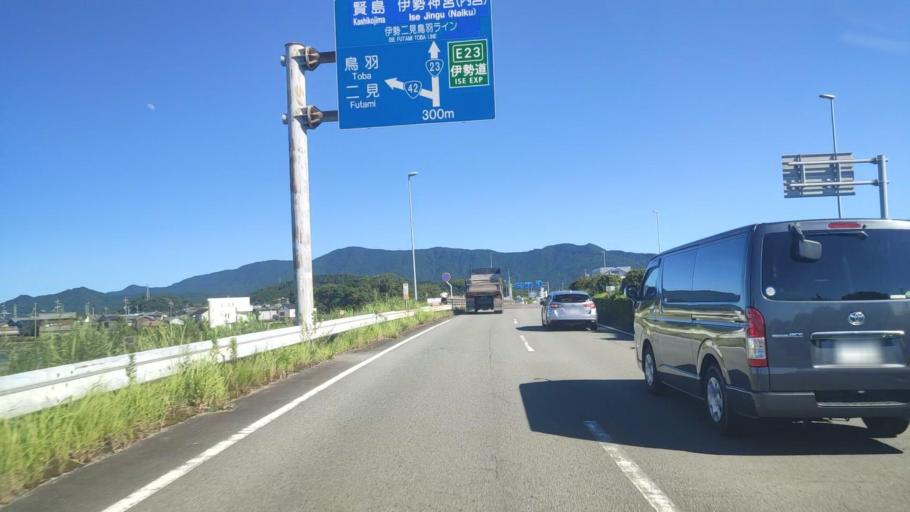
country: JP
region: Mie
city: Ise
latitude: 34.5034
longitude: 136.7377
